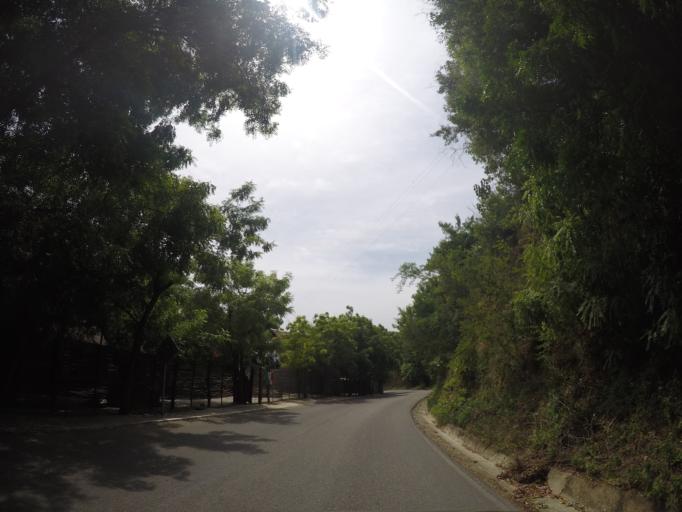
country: MX
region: Oaxaca
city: Santa Maria Tonameca
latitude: 15.6668
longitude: -96.5365
